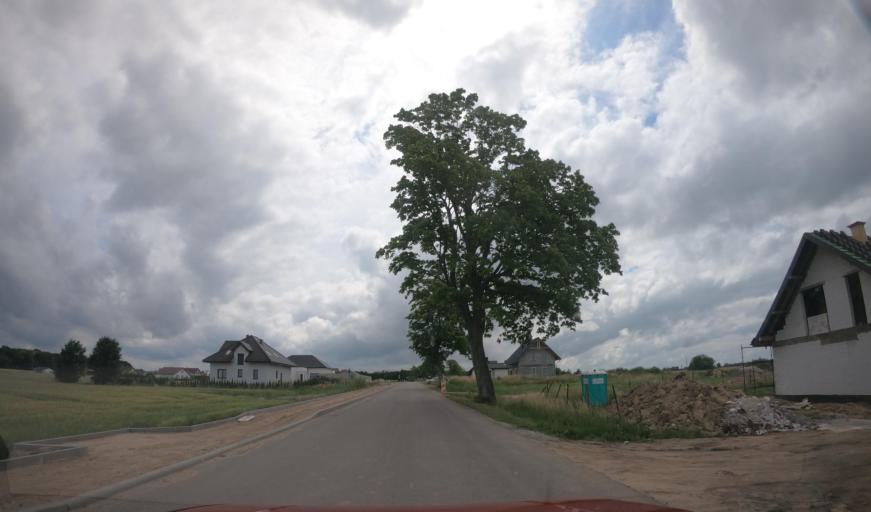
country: PL
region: West Pomeranian Voivodeship
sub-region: Powiat koszalinski
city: Mielno
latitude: 54.2266
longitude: 16.1045
